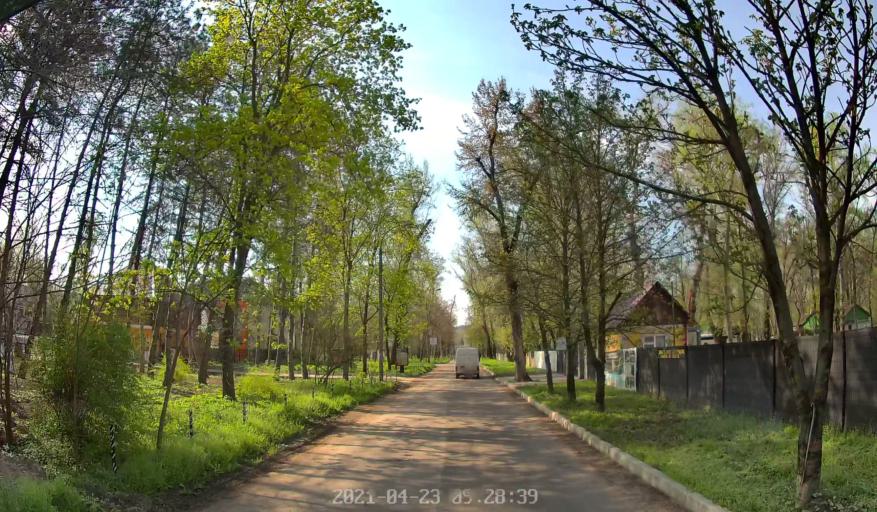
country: MD
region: Chisinau
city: Vadul lui Voda
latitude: 47.0861
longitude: 29.1083
